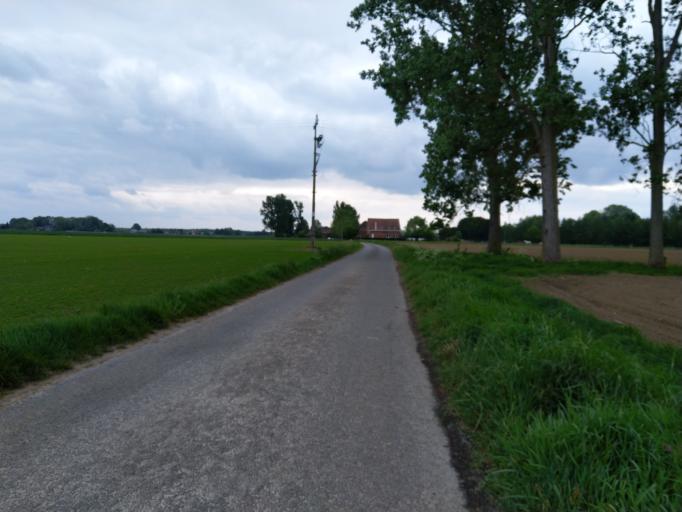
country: BE
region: Wallonia
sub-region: Province du Hainaut
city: Jurbise
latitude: 50.5247
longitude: 3.8846
